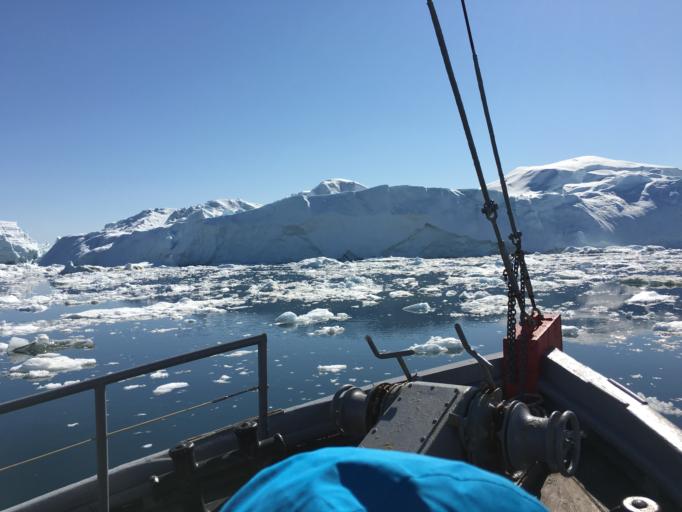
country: GL
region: Qaasuitsup
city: Ilulissat
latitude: 69.2027
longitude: -51.1605
